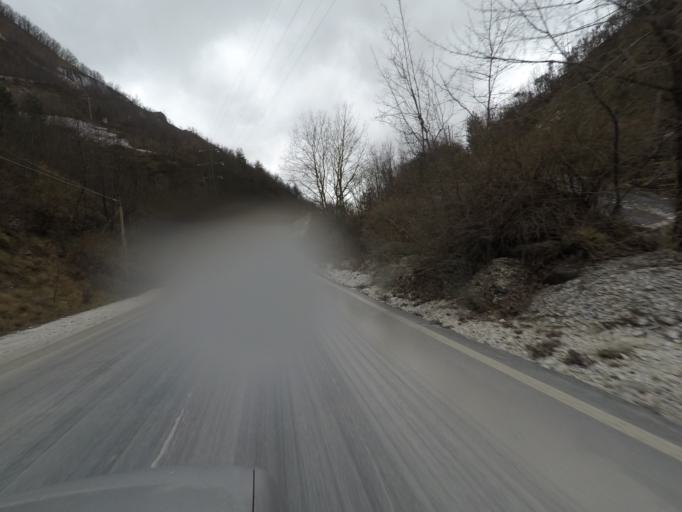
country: IT
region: Tuscany
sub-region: Provincia di Massa-Carrara
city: Montignoso
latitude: 44.0829
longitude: 10.1499
